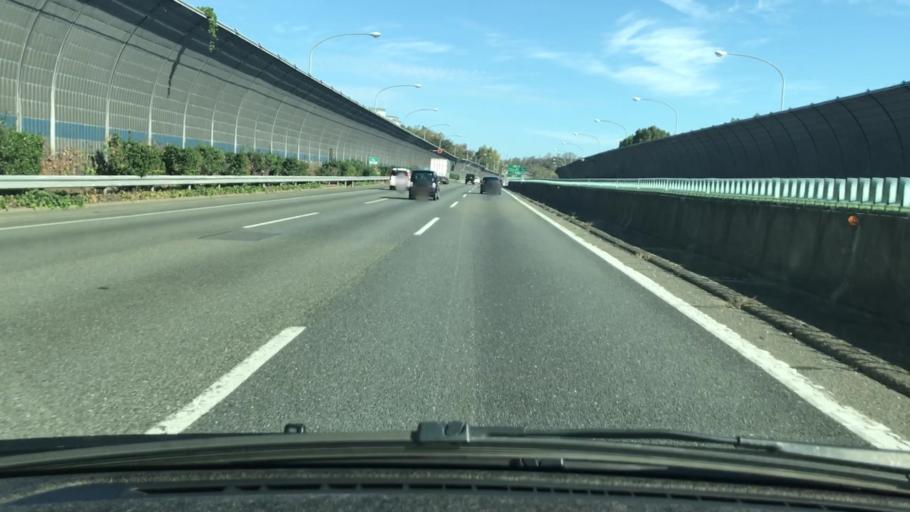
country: JP
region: Osaka
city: Ibaraki
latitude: 34.8489
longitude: 135.5800
